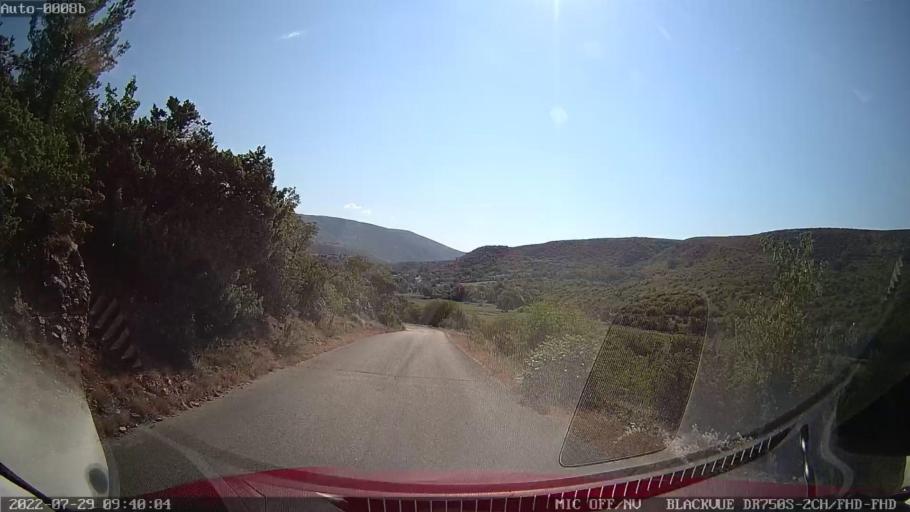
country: HR
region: Zadarska
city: Obrovac
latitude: 44.1936
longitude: 15.7610
